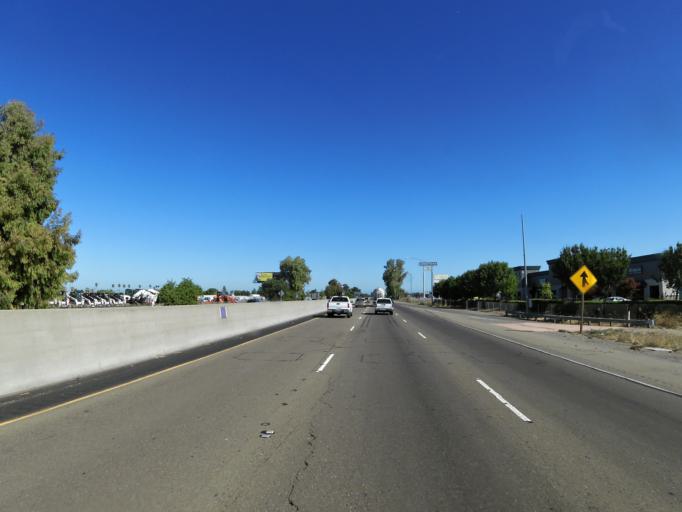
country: US
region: California
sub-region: San Joaquin County
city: August
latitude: 37.9937
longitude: -121.2533
